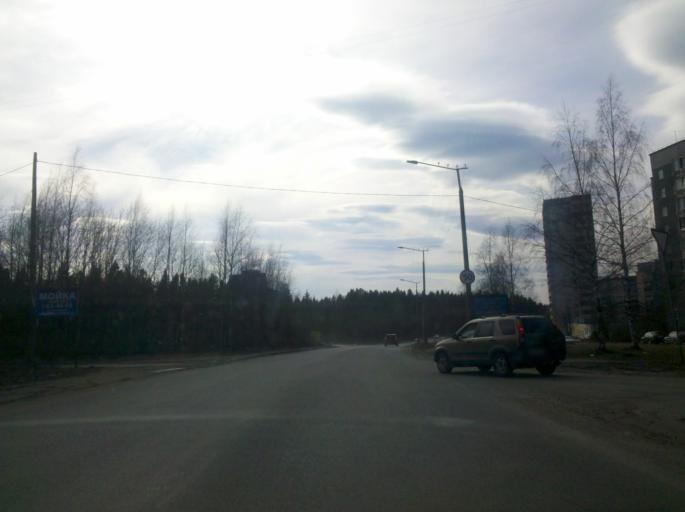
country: RU
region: Republic of Karelia
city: Petrozavodsk
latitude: 61.7577
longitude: 34.3732
